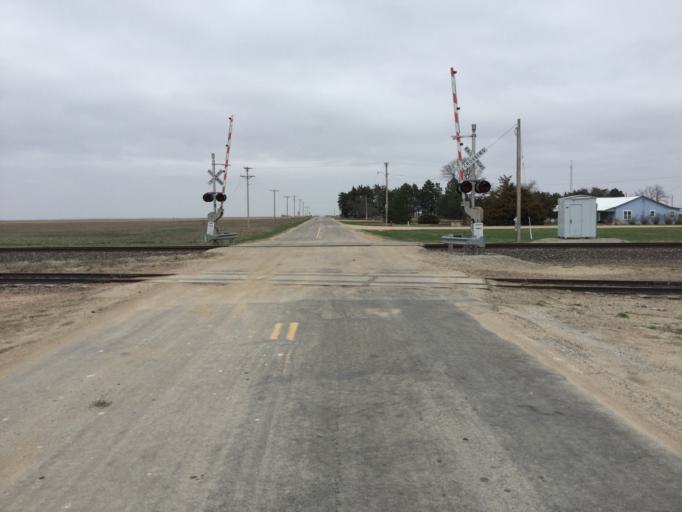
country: US
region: Kansas
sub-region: Russell County
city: Russell
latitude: 38.8756
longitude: -98.7066
